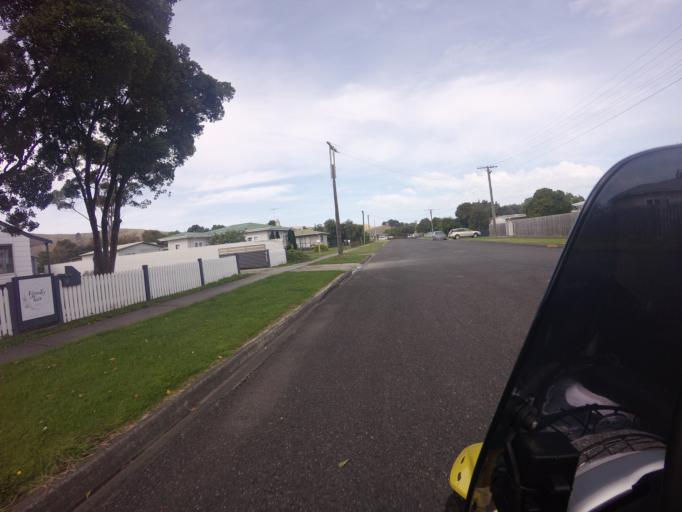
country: NZ
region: Gisborne
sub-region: Gisborne District
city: Gisborne
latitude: -38.6851
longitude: 178.0568
